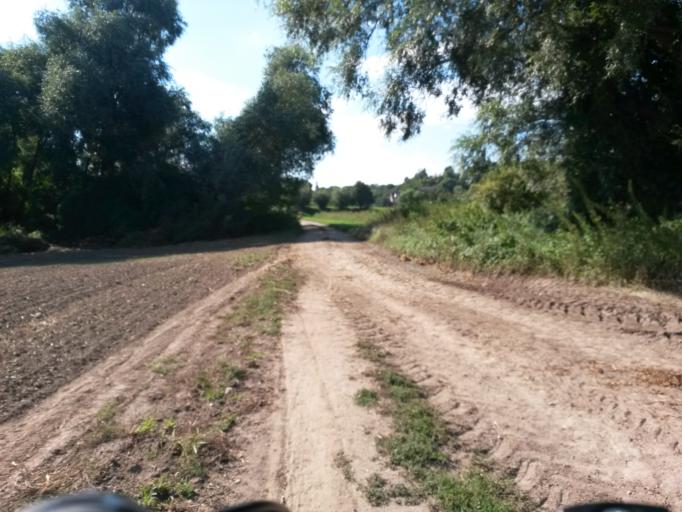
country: DE
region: Brandenburg
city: Schoneberg
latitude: 52.9496
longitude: 14.1134
